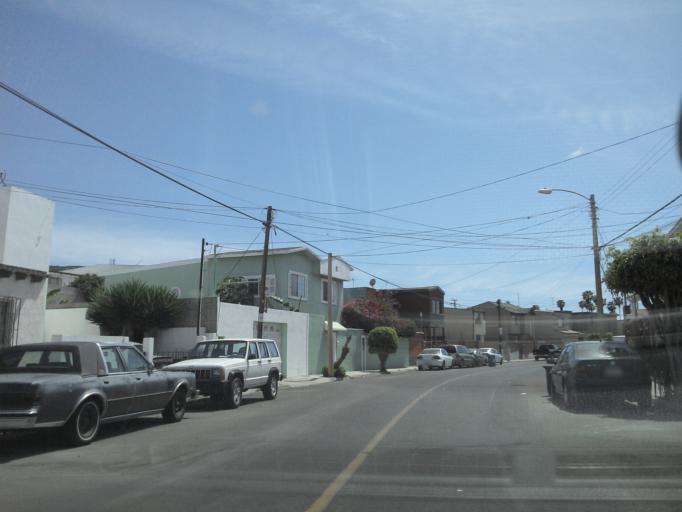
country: MX
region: Baja California
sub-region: Tijuana
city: La Esperanza [Granjas Familiares]
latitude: 32.5080
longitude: -117.1191
